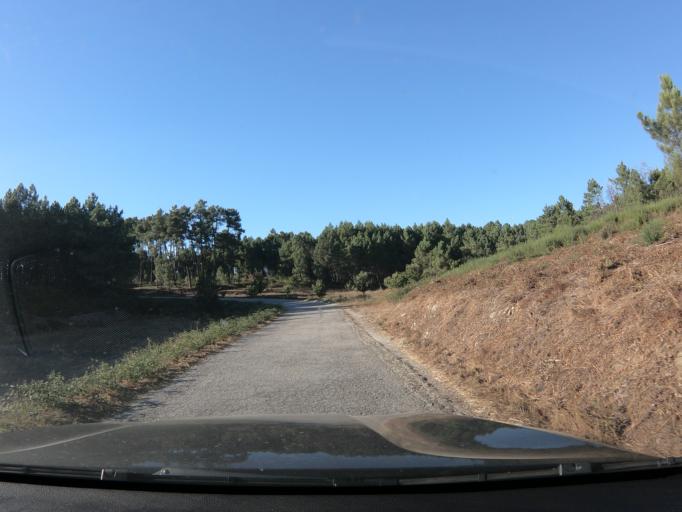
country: PT
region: Vila Real
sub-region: Sabrosa
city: Vilela
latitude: 41.2525
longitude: -7.6378
